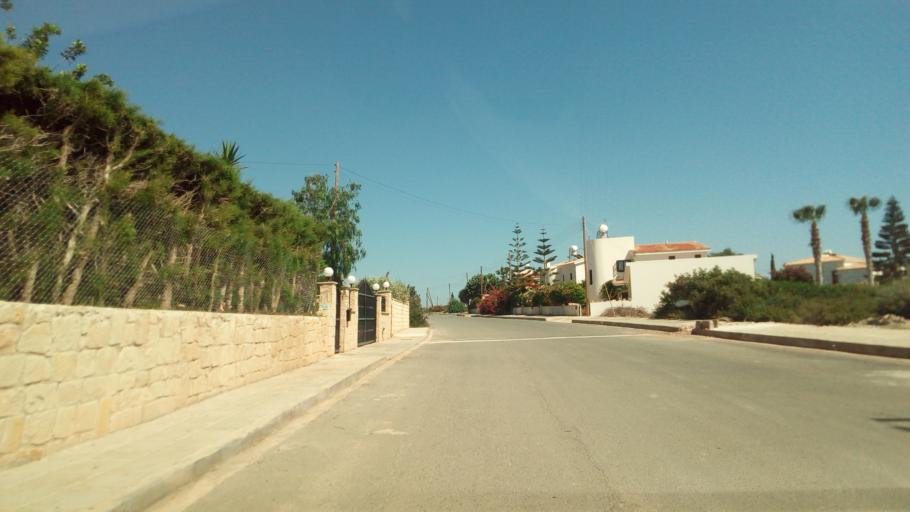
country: CY
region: Pafos
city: Pegeia
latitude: 34.8889
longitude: 32.3332
